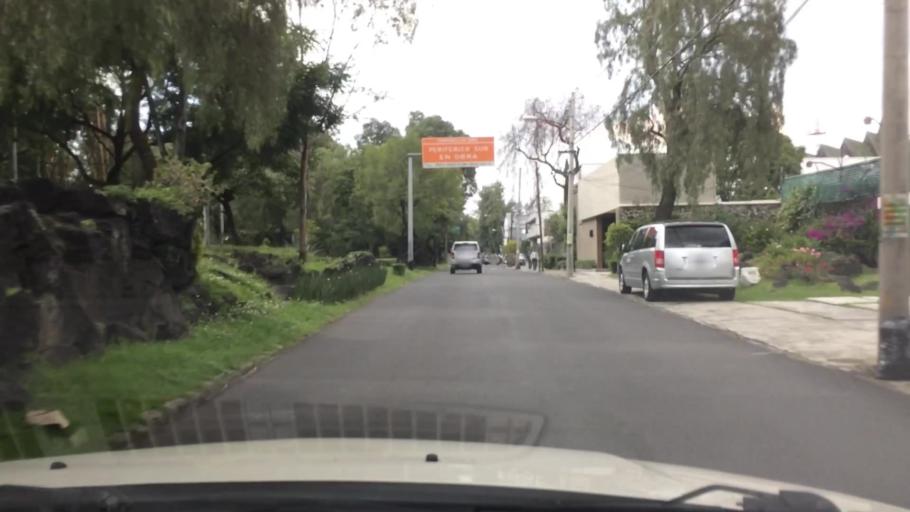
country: MX
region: Mexico City
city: Magdalena Contreras
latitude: 19.3143
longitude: -99.2119
